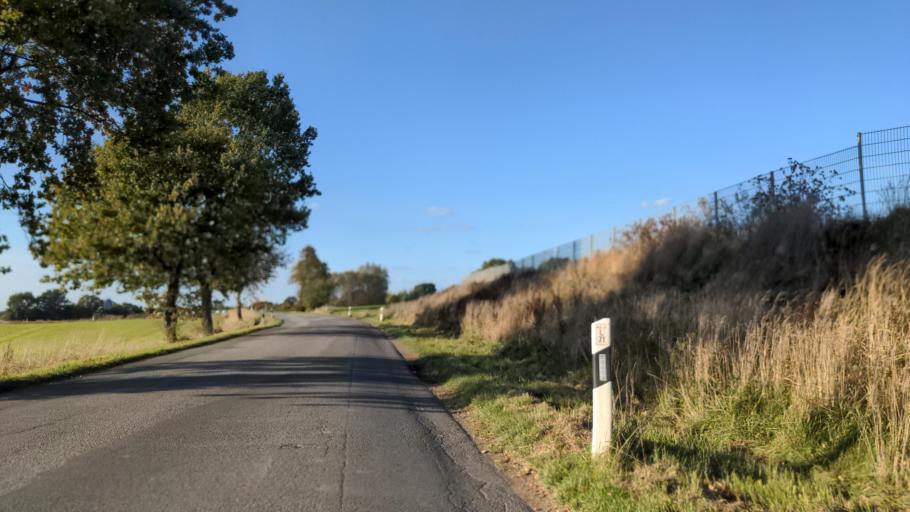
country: DE
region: Schleswig-Holstein
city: Strukdorf
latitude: 53.9575
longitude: 10.5268
